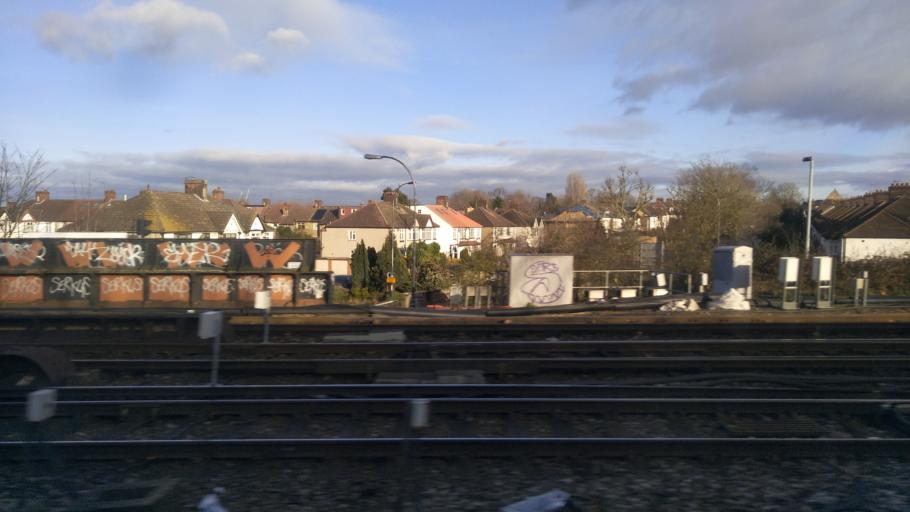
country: GB
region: England
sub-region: Greater London
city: Blackheath
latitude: 51.4454
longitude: 0.0057
